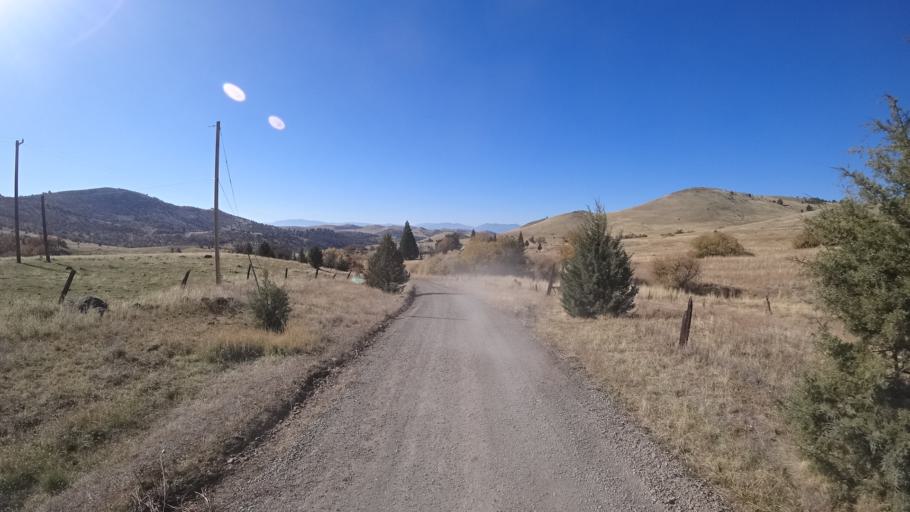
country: US
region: California
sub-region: Siskiyou County
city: Montague
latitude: 41.7998
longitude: -122.3298
